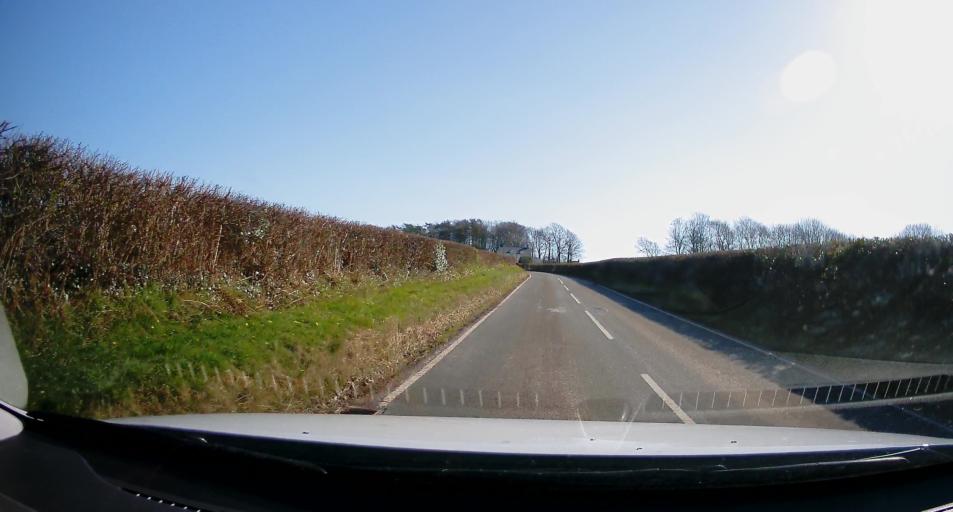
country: GB
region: Wales
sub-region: County of Ceredigion
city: Penparcau
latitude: 52.3572
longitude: -4.0578
